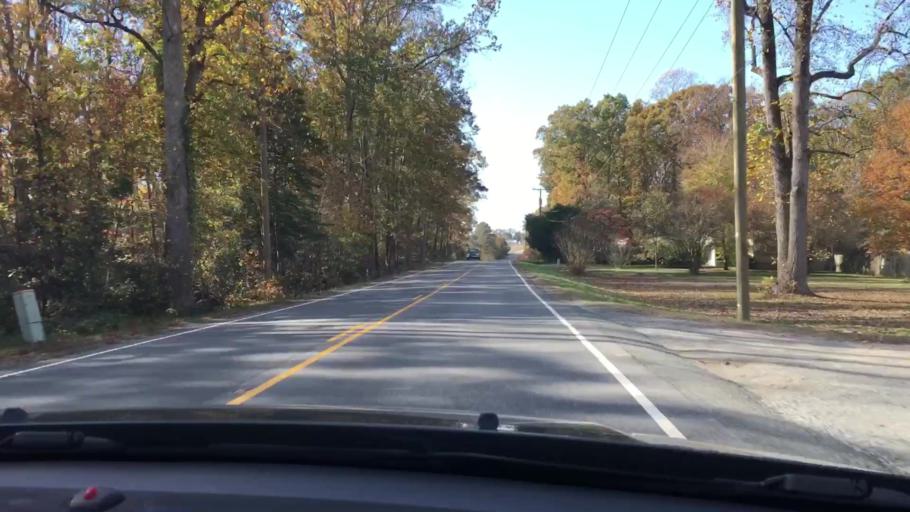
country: US
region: Virginia
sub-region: King and Queen County
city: King and Queen Court House
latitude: 37.5911
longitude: -76.8774
